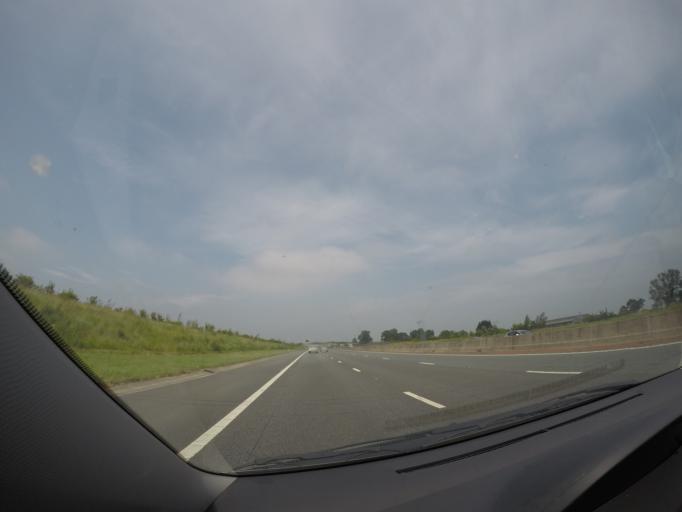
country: GB
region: England
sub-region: North Yorkshire
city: Bedale
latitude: 54.2633
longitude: -1.5183
